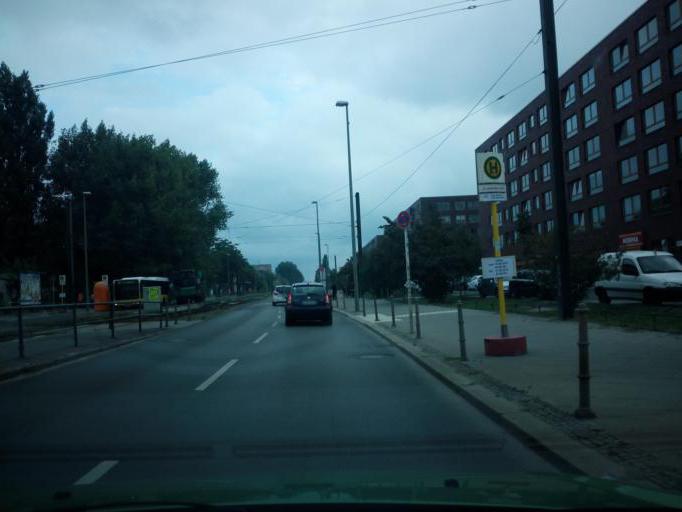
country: DE
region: Berlin
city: Rummelsburg
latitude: 52.5011
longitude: 13.4760
